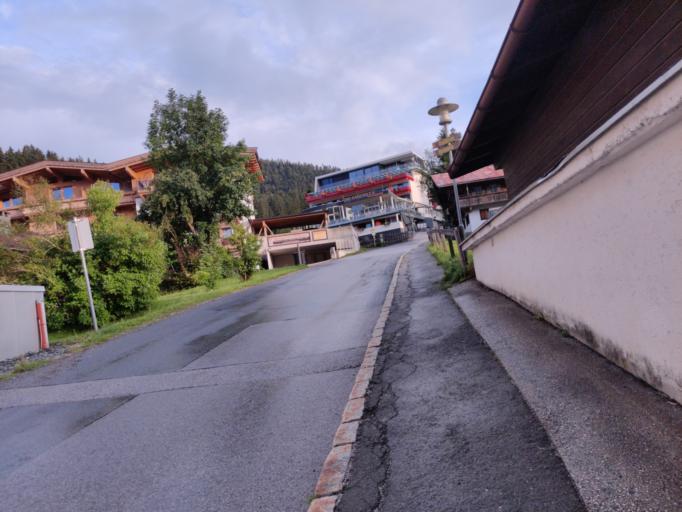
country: AT
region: Tyrol
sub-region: Politischer Bezirk Kufstein
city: Ellmau
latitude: 47.5121
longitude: 12.3018
